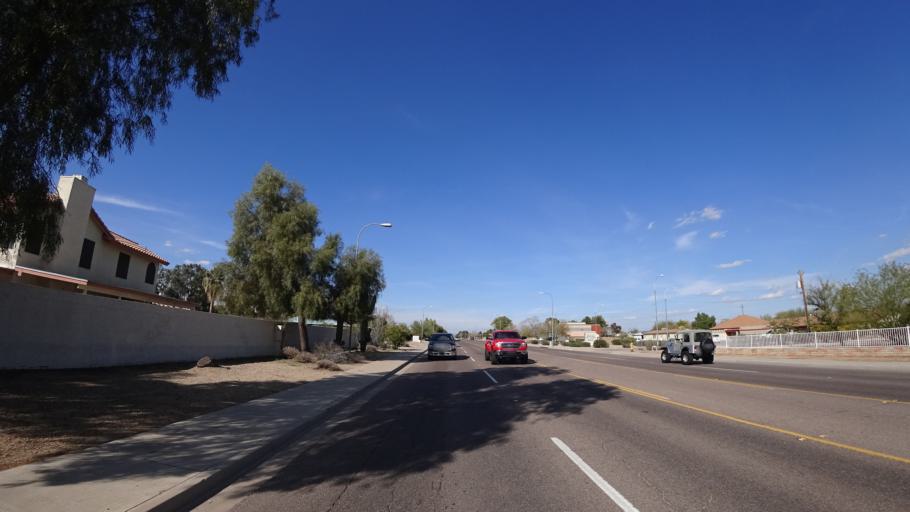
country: US
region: Arizona
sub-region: Maricopa County
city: Peoria
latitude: 33.6155
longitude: -112.2201
